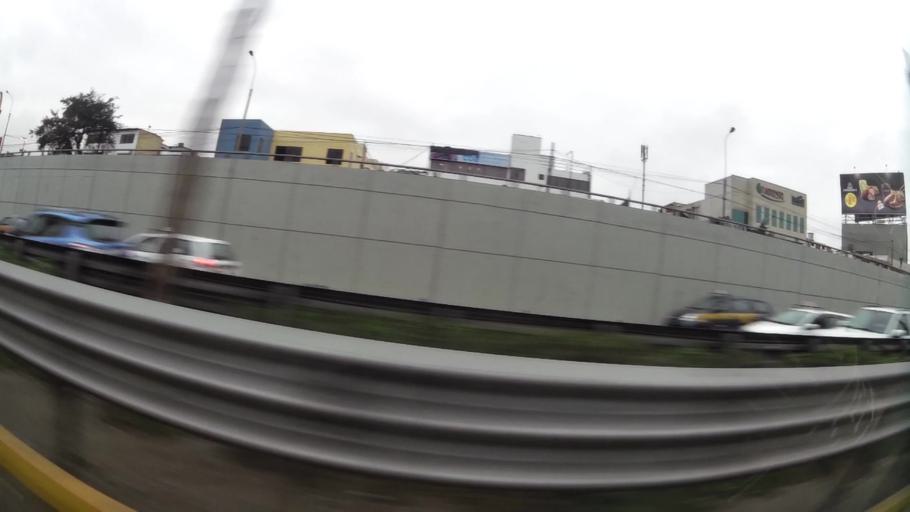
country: PE
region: Lima
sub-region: Lima
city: San Luis
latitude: -12.0888
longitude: -77.0089
